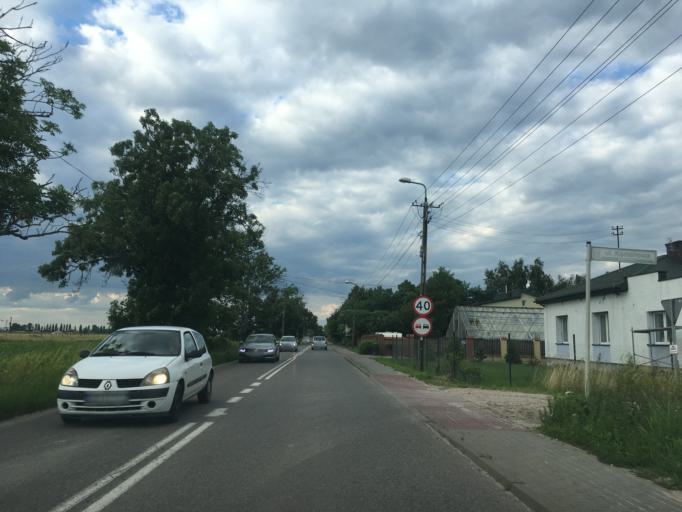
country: PL
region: Masovian Voivodeship
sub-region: Powiat piaseczynski
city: Lesznowola
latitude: 52.0948
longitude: 20.9730
